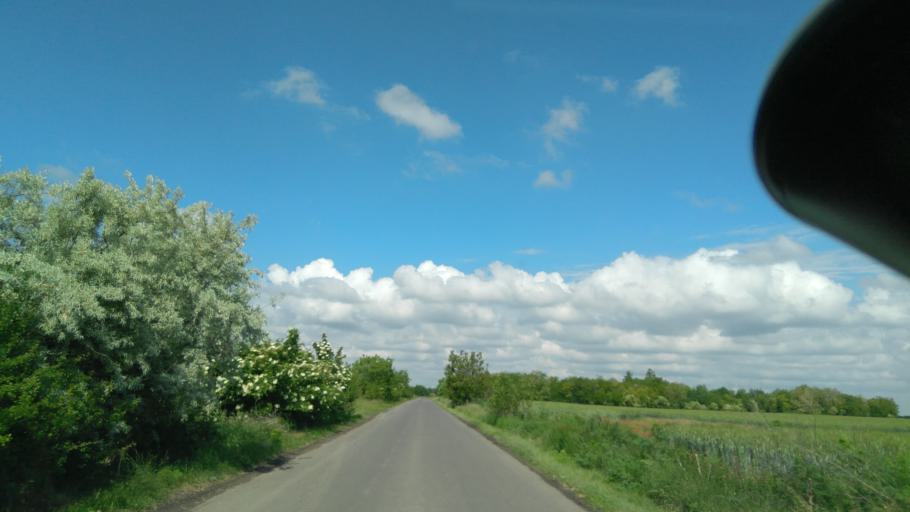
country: HU
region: Bekes
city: Bekes
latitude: 46.8199
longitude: 21.1441
